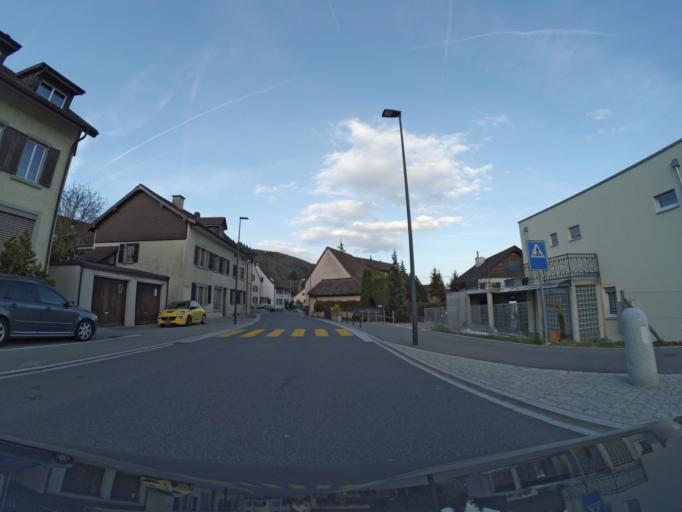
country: CH
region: Schaffhausen
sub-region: Bezirk Schaffhausen
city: Beringen
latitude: 47.6979
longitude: 8.5714
